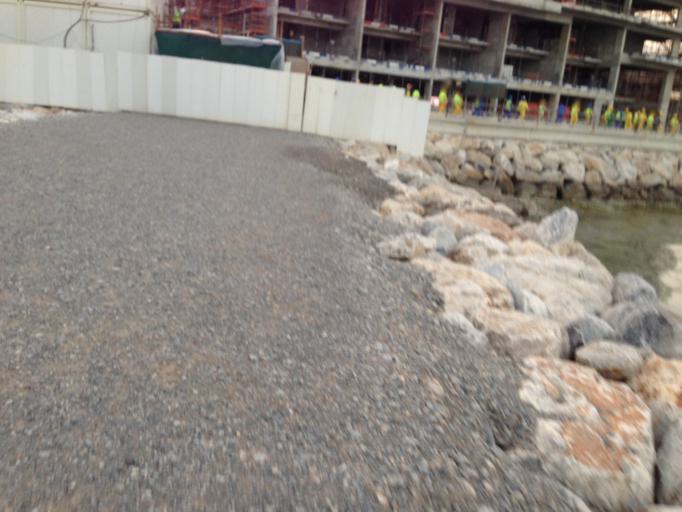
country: OM
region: Muhafazat Masqat
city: As Sib al Jadidah
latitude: 23.6288
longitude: 58.2740
